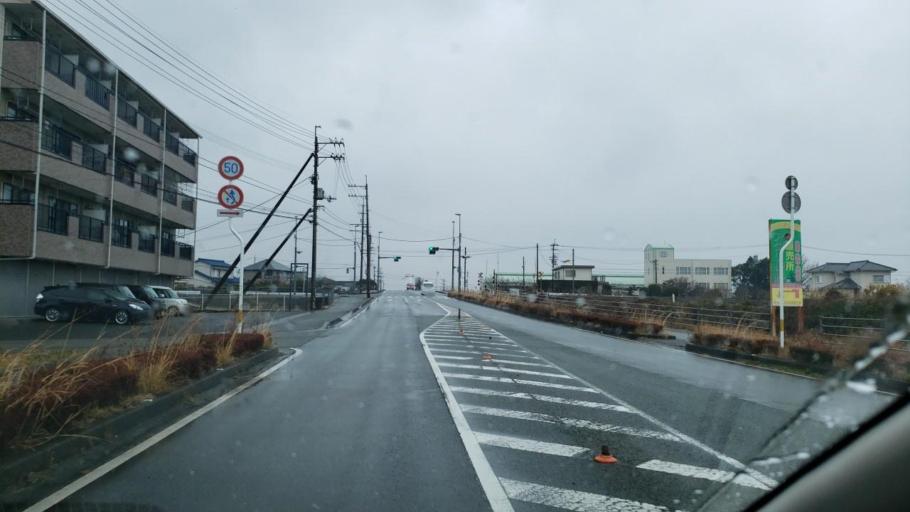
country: JP
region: Tokushima
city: Ishii
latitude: 34.1469
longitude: 134.4763
